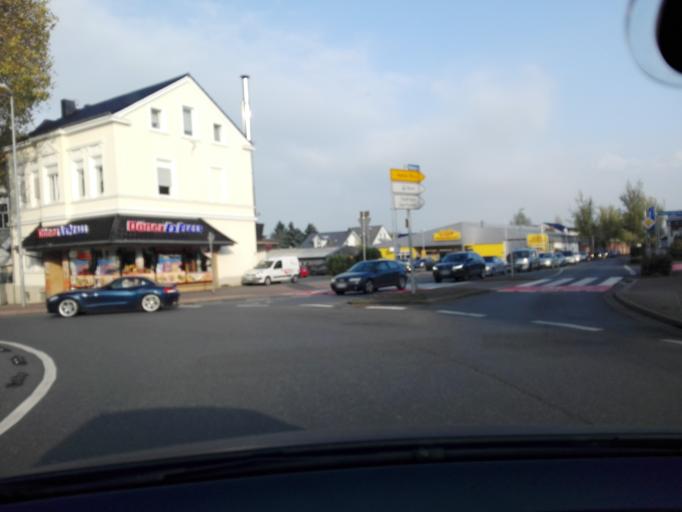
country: DE
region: North Rhine-Westphalia
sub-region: Regierungsbezirk Arnsberg
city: Unna
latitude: 51.5410
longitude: 7.6880
